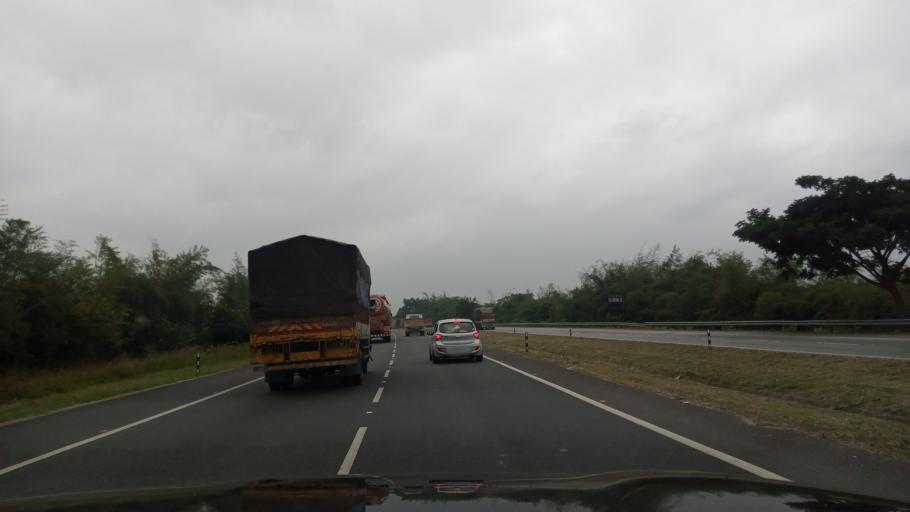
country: IN
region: Karnataka
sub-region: Bangalore Rural
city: Nelamangala
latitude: 13.0306
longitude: 77.4756
